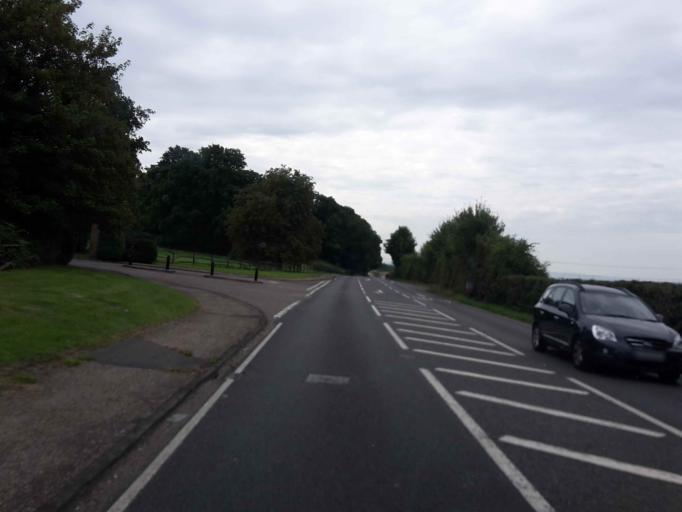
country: GB
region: England
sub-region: West Sussex
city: Billingshurst
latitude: 51.0349
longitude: -0.4426
